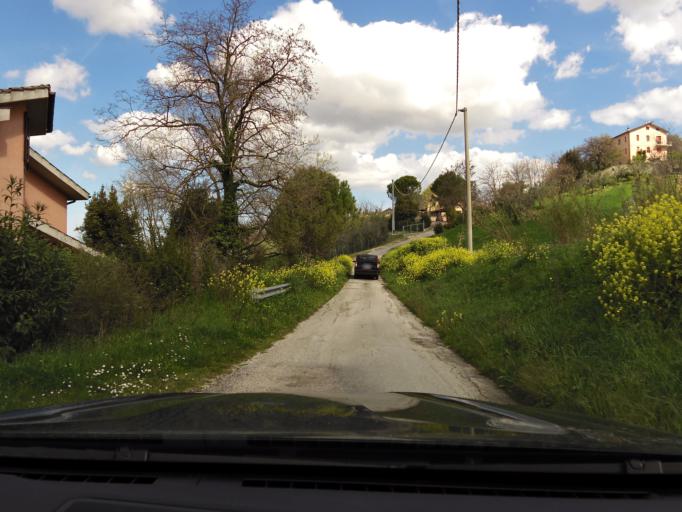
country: IT
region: The Marches
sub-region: Provincia di Ancona
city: Castelfidardo
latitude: 43.4703
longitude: 13.5468
